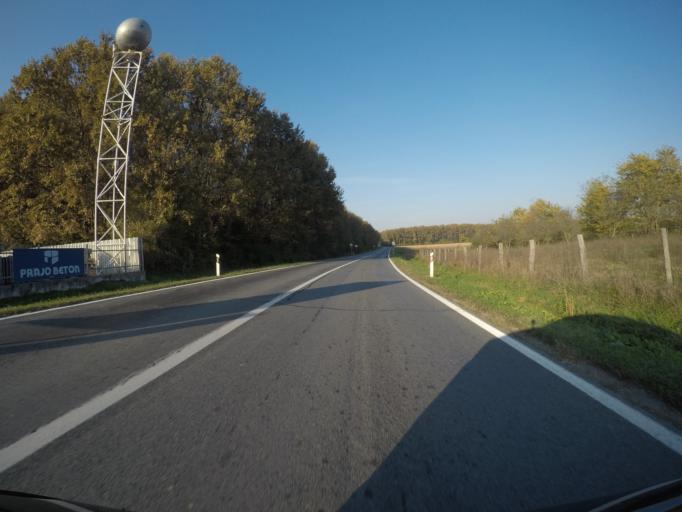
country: HR
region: Virovitick-Podravska
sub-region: Grad Virovitica
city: Virovitica
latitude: 45.8780
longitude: 17.4053
